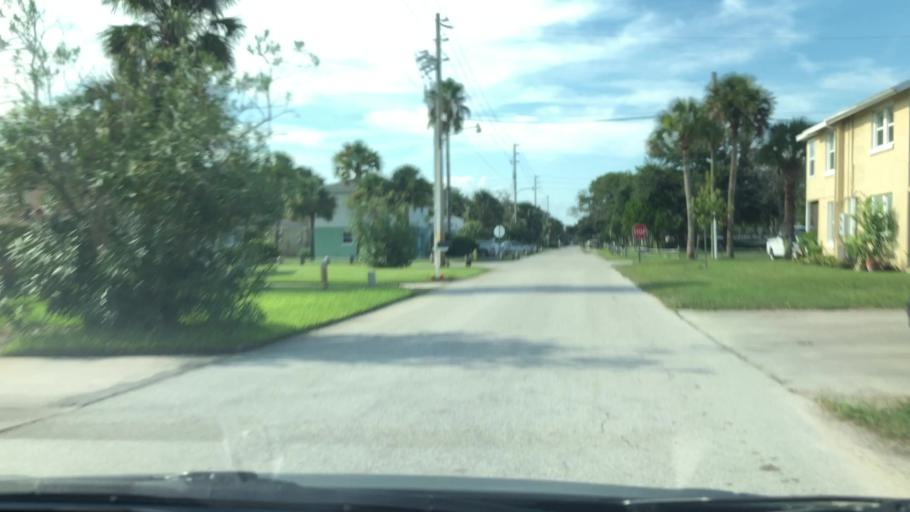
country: US
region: Florida
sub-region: Duval County
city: Jacksonville Beach
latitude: 30.2948
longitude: -81.3954
